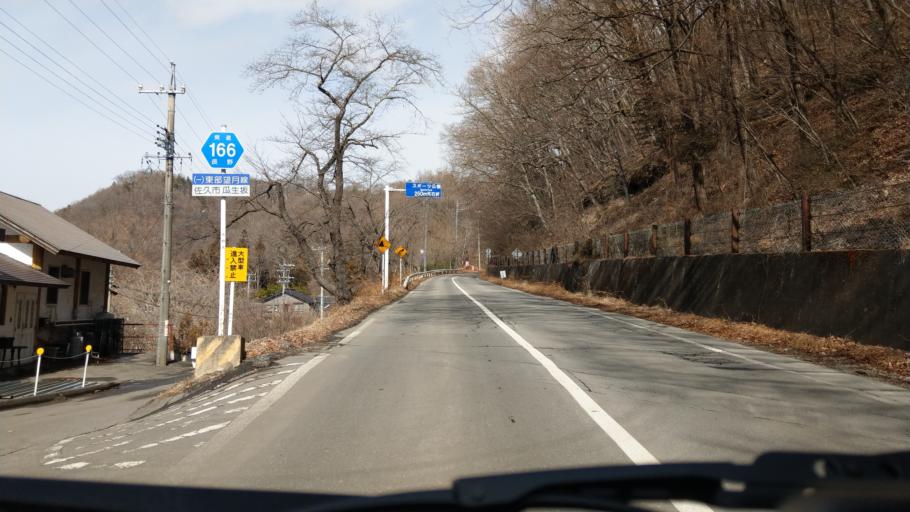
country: JP
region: Nagano
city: Komoro
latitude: 36.2628
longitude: 138.3659
